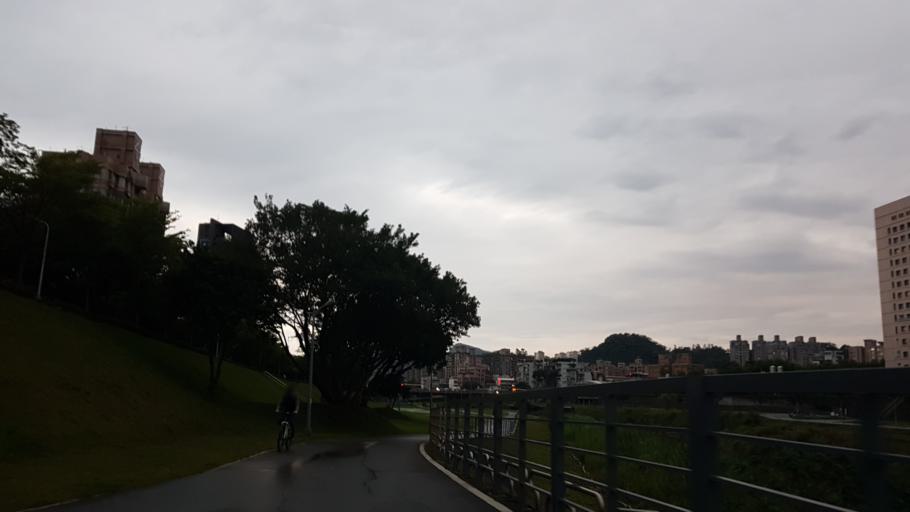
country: TW
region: Taipei
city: Taipei
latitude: 24.9849
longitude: 121.5715
